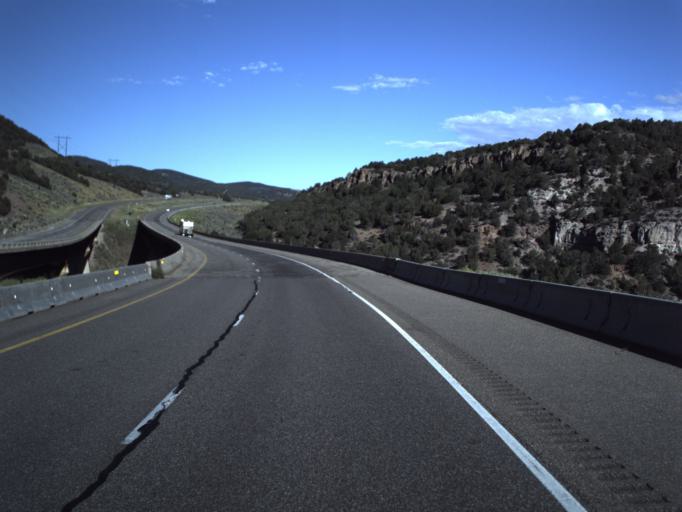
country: US
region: Utah
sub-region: Sevier County
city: Monroe
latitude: 38.5633
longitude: -112.4296
